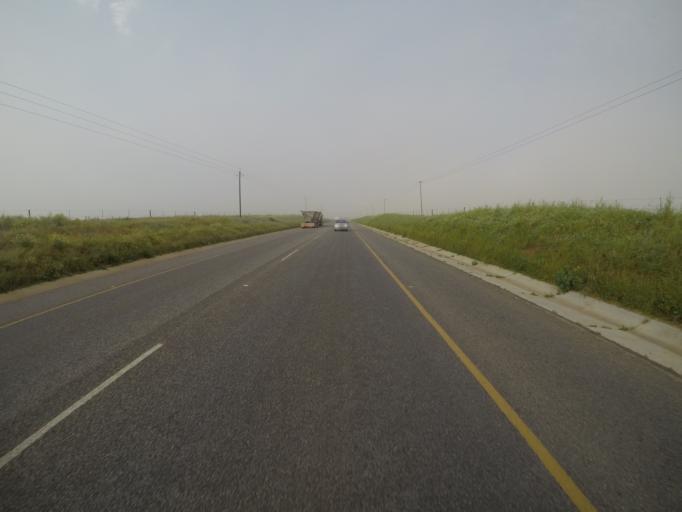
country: ZA
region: Western Cape
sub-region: West Coast District Municipality
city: Malmesbury
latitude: -33.6409
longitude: 18.7162
